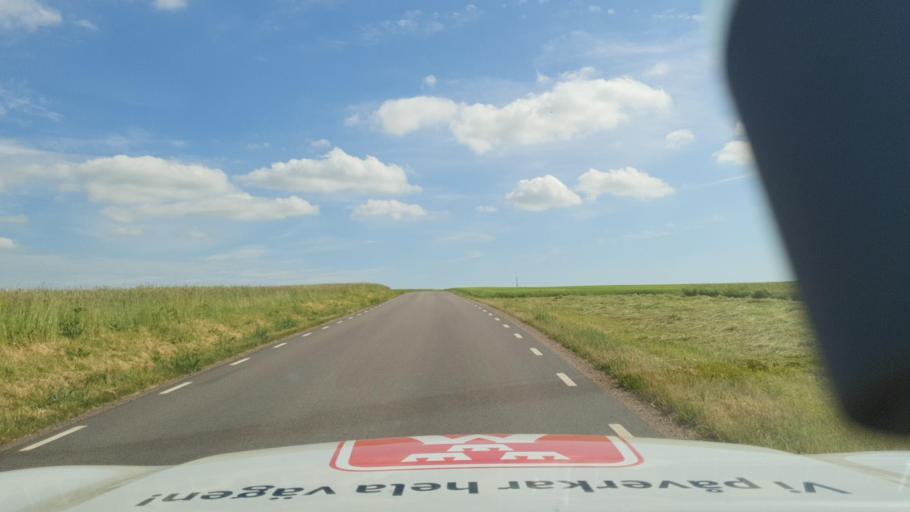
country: SE
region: Skane
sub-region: Sjobo Kommun
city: Blentarp
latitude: 55.5582
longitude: 13.5614
